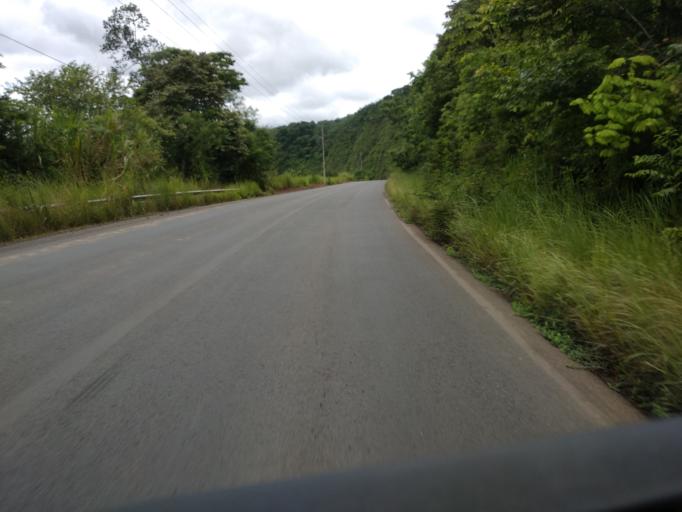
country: CR
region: Puntarenas
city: Buenos Aires
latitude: 9.0895
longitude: -83.2716
